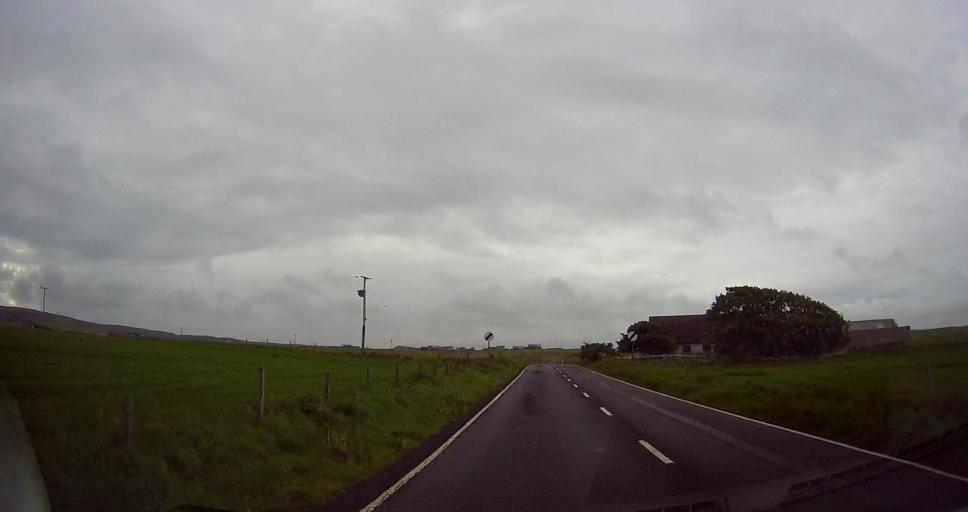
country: GB
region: Scotland
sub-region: Orkney Islands
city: Stromness
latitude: 59.0337
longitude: -3.1849
